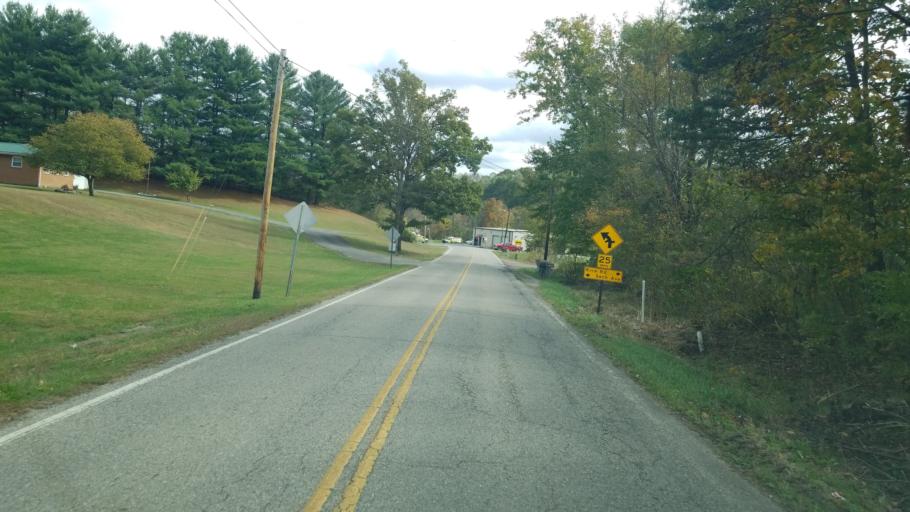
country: US
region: Ohio
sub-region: Jackson County
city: Jackson
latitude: 39.0726
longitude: -82.5756
